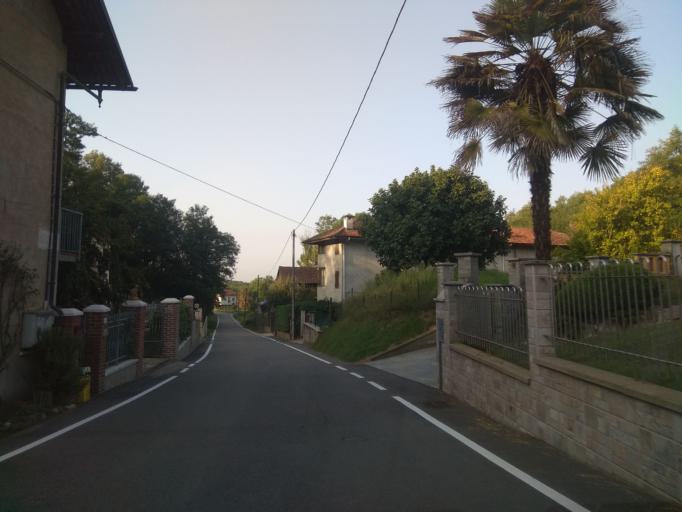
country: IT
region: Piedmont
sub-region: Provincia di Vercelli
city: San Maurizio
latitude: 45.6066
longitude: 8.3022
